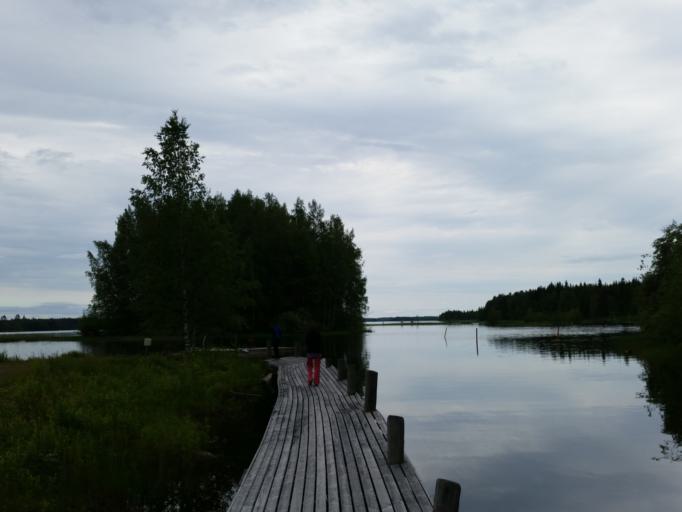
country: FI
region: Northern Savo
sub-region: Sisae-Savo
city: Tervo
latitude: 63.0049
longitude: 26.6908
